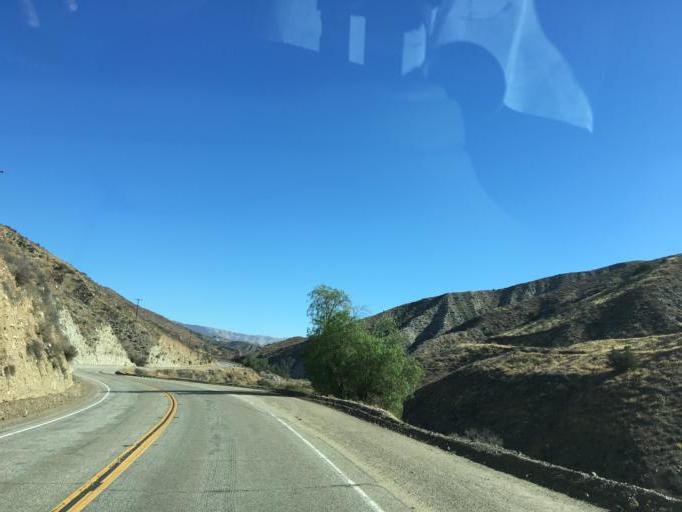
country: US
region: California
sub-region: Los Angeles County
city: Agua Dulce
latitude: 34.4399
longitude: -118.3333
